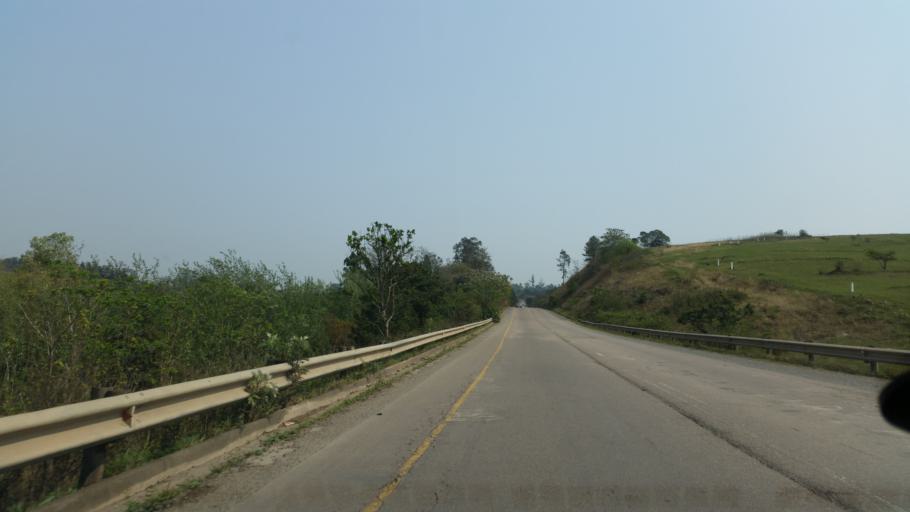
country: ZA
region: KwaZulu-Natal
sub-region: eThekwini Metropolitan Municipality
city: Mpumalanga
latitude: -29.7376
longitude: 30.6583
